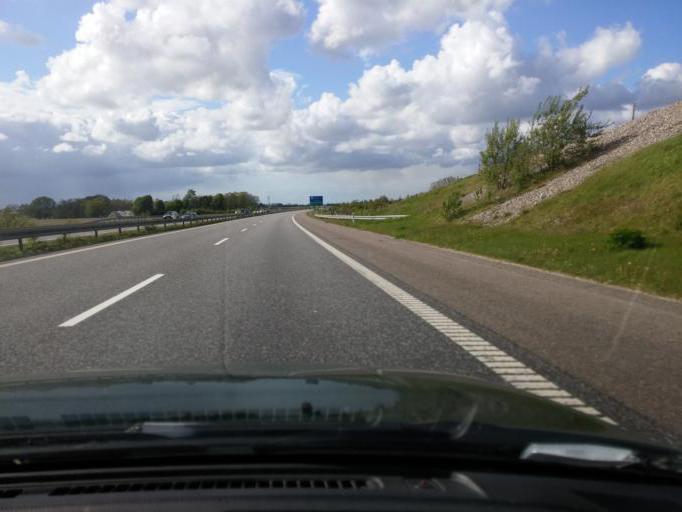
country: DK
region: South Denmark
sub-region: Faaborg-Midtfyn Kommune
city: Arslev
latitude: 55.2864
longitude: 10.4476
